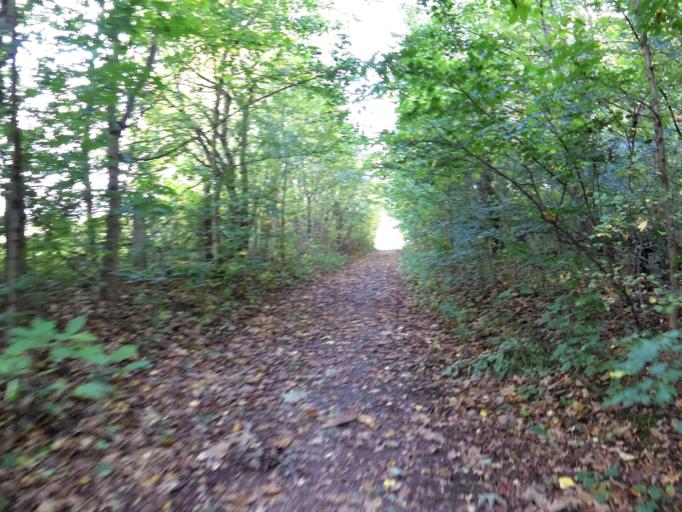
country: DE
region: Saxony
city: Grossposna
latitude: 51.2905
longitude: 12.4911
